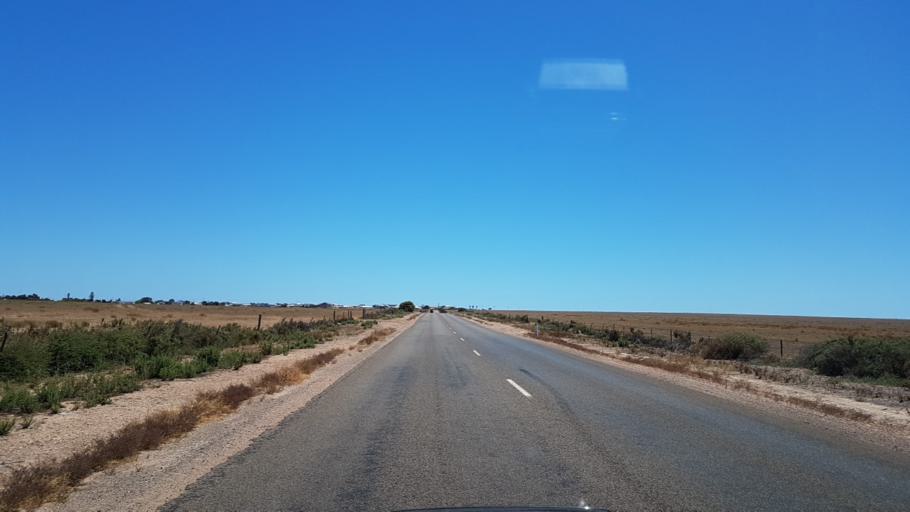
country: AU
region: South Australia
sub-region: Copper Coast
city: Wallaroo
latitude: -33.9053
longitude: 137.6393
